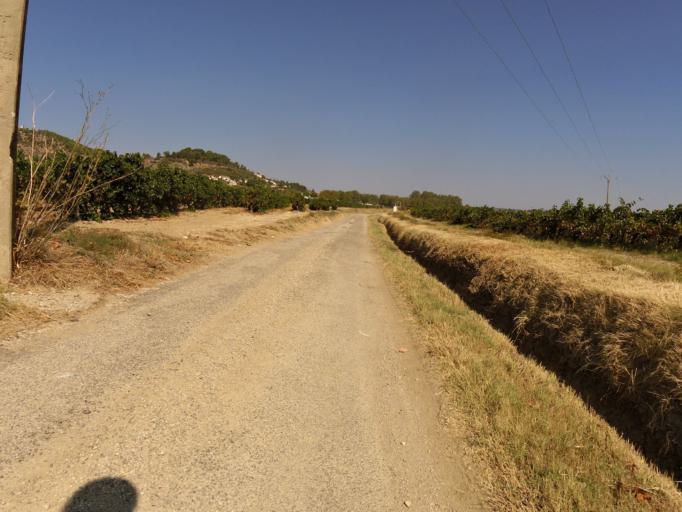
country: FR
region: Languedoc-Roussillon
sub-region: Departement du Gard
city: Calvisson
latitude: 43.7735
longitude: 4.1916
